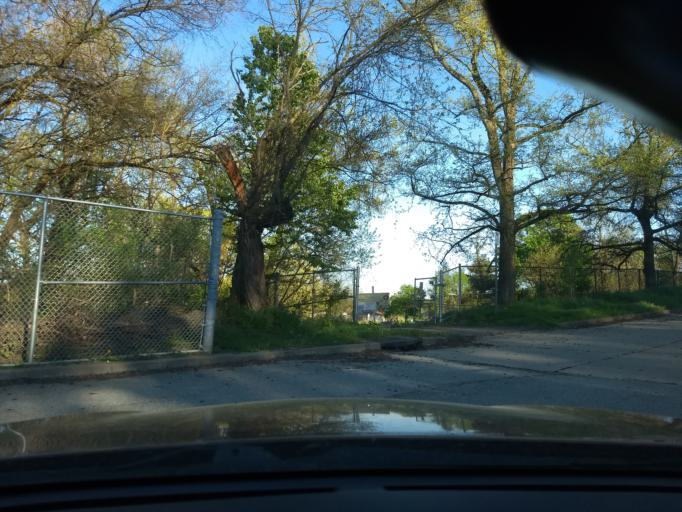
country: US
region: Pennsylvania
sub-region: Allegheny County
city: Dormont
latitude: 40.4152
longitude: -80.0204
